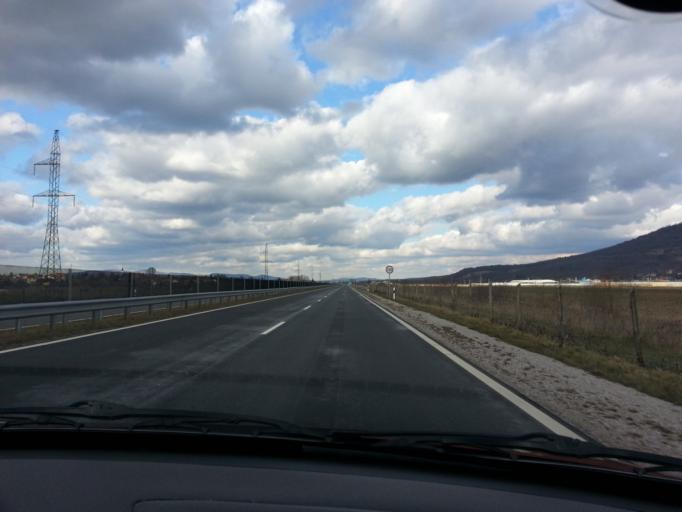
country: HU
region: Nograd
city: Jobbagyi
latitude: 47.8193
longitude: 19.6794
